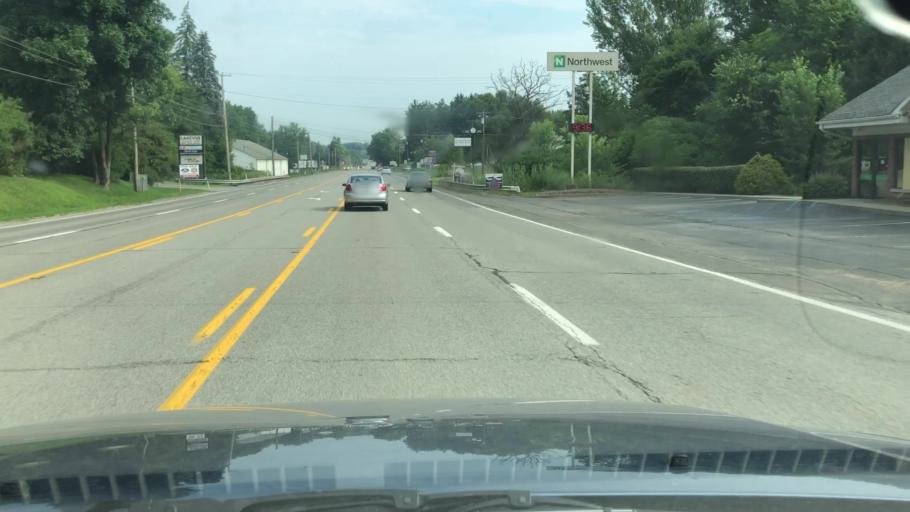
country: US
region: Pennsylvania
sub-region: Allegheny County
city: Bakerstown
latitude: 40.6764
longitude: -79.9334
